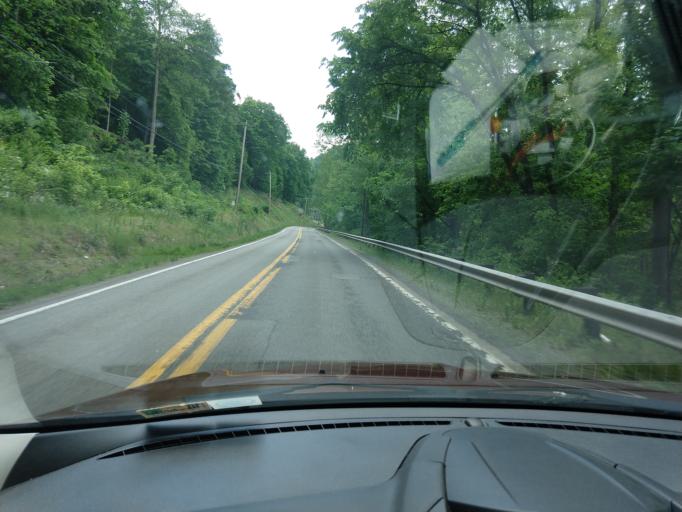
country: US
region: West Virginia
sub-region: Gilmer County
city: Glenville
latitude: 38.8701
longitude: -80.6995
